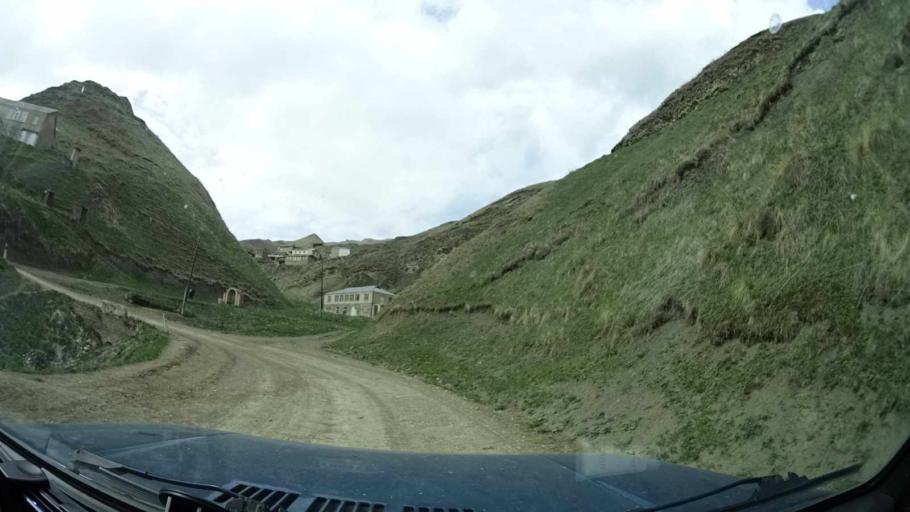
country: RU
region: Dagestan
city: Usisha
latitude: 42.1347
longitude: 47.3645
